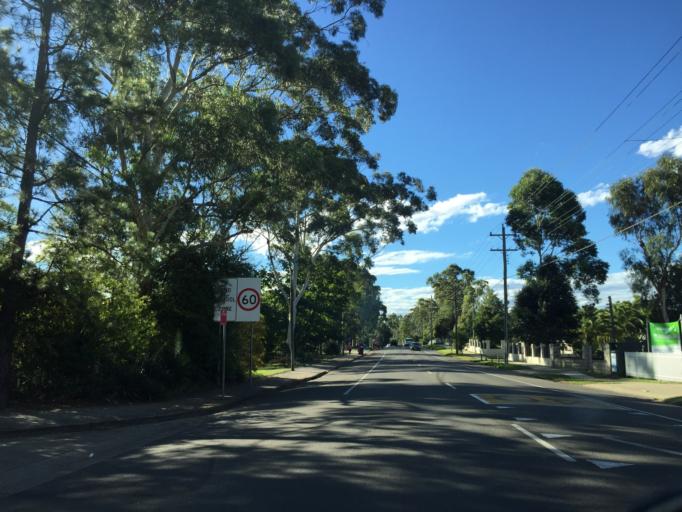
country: AU
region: New South Wales
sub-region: The Hills Shire
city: Glenhaven
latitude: -33.6995
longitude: 151.0029
